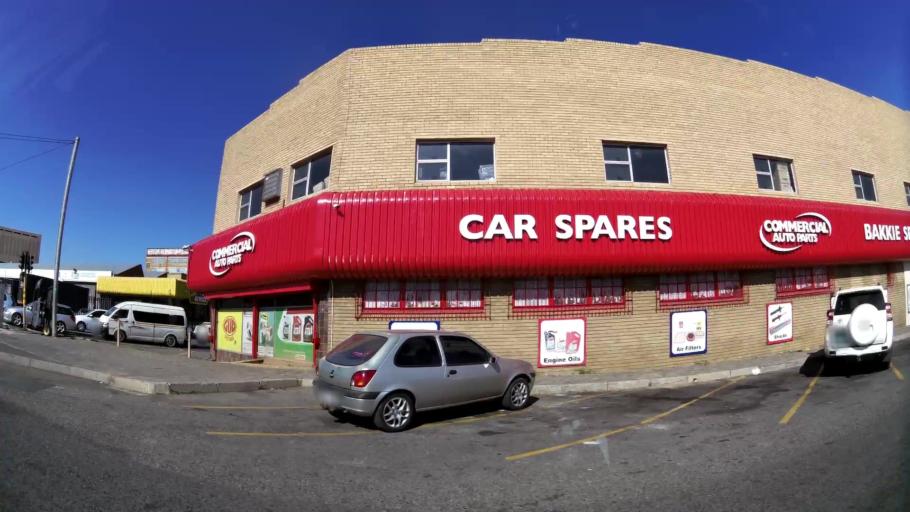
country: ZA
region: Gauteng
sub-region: City of Johannesburg Metropolitan Municipality
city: Johannesburg
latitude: -26.2137
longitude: 28.0348
